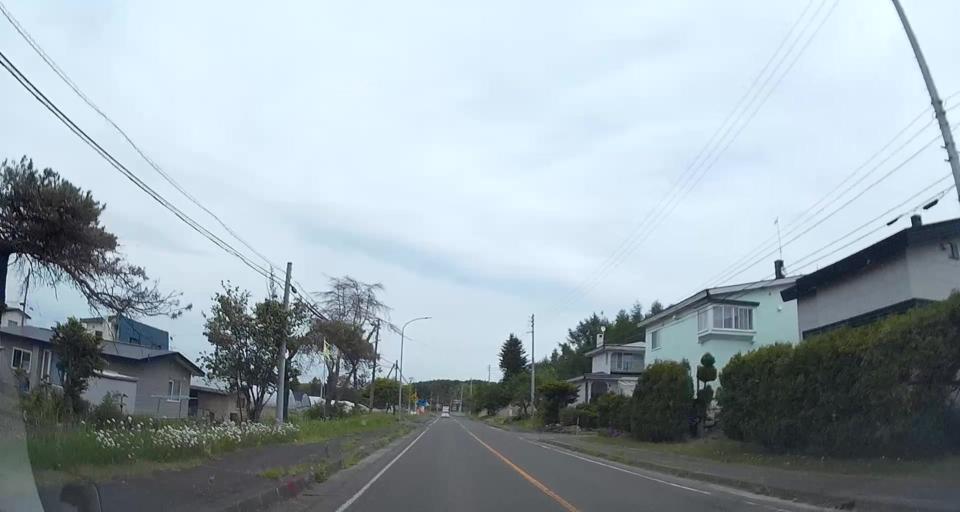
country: JP
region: Hokkaido
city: Chitose
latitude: 42.7728
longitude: 141.8320
